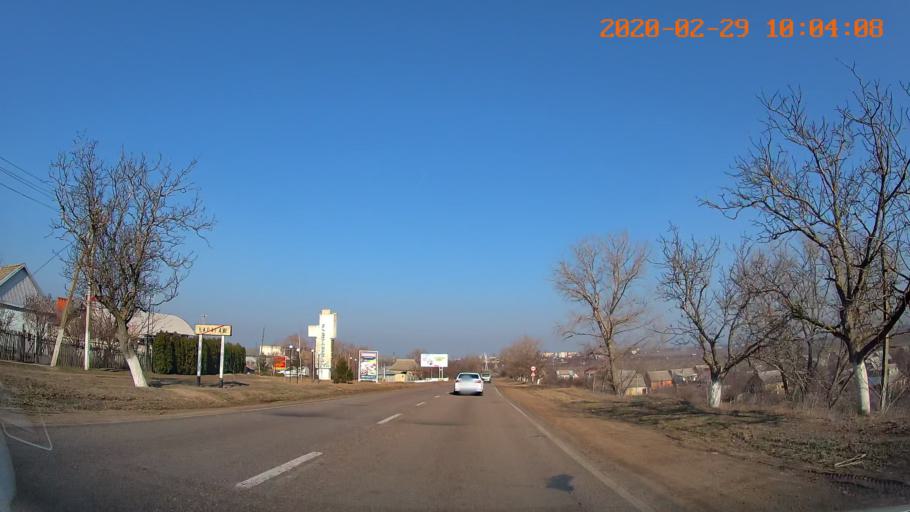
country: MD
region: Causeni
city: Chitcani
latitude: 46.7957
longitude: 29.6770
